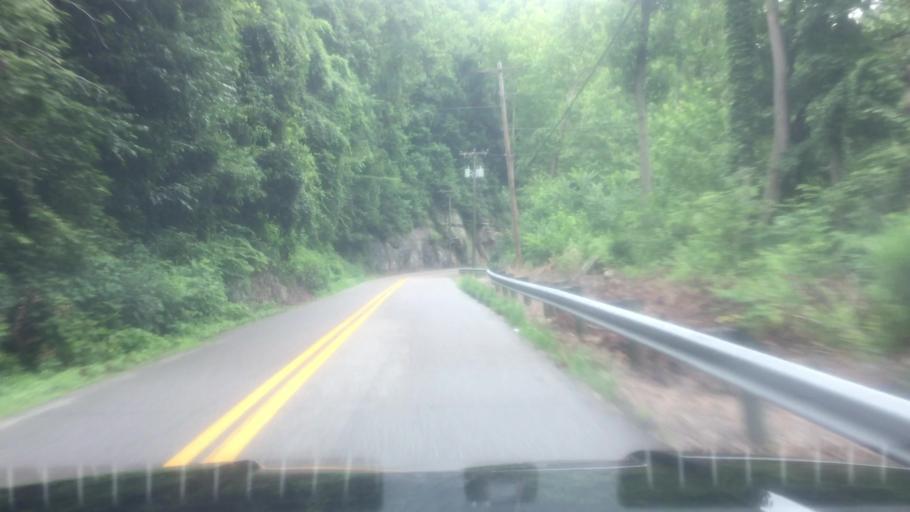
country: US
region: West Virginia
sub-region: Kanawha County
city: Montgomery
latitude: 38.1043
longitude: -81.3830
